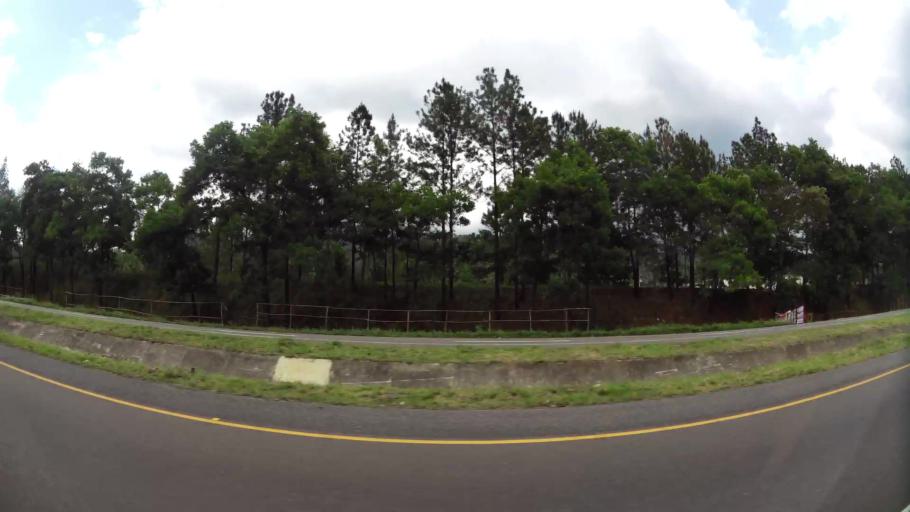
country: DO
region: Monsenor Nouel
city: Juan Adrian
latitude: 18.7887
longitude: -70.2681
